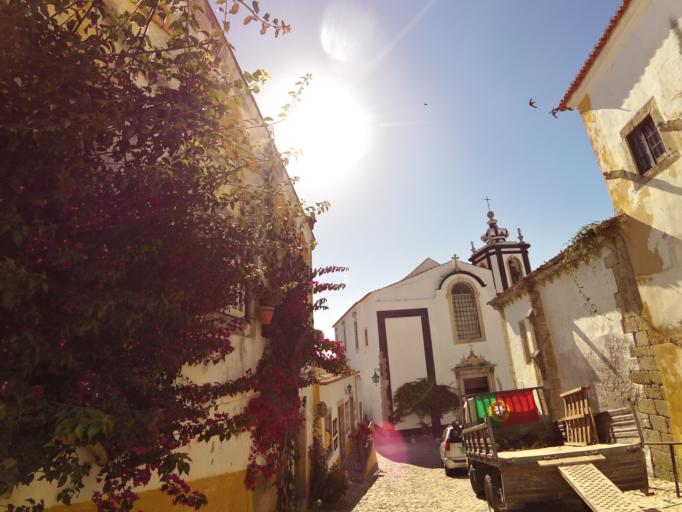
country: PT
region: Leiria
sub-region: Obidos
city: Obidos
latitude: 39.3609
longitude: -9.1575
